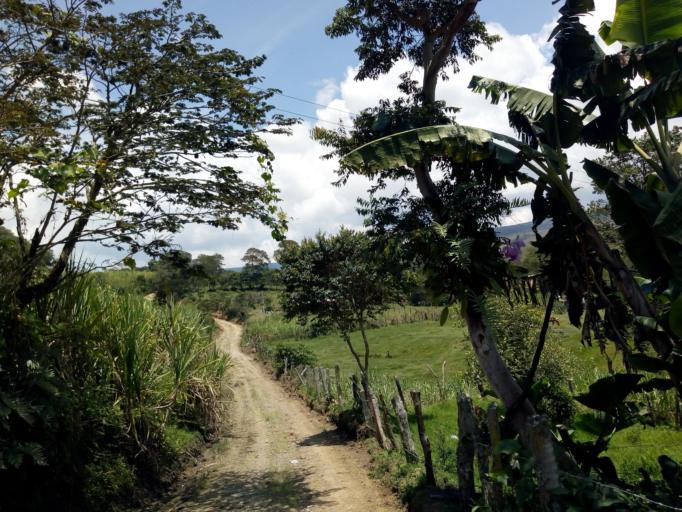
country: CO
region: Boyaca
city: Moniquira
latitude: 5.8697
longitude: -73.5070
